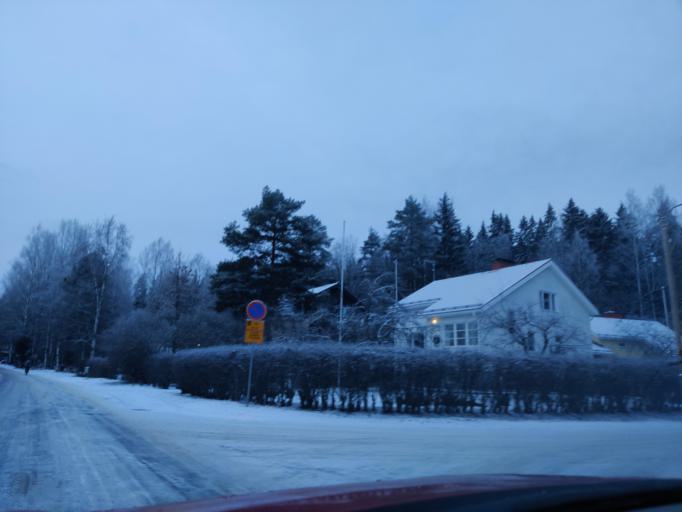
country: FI
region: Pirkanmaa
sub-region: Tampere
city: Tampere
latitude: 61.5074
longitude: 23.8025
